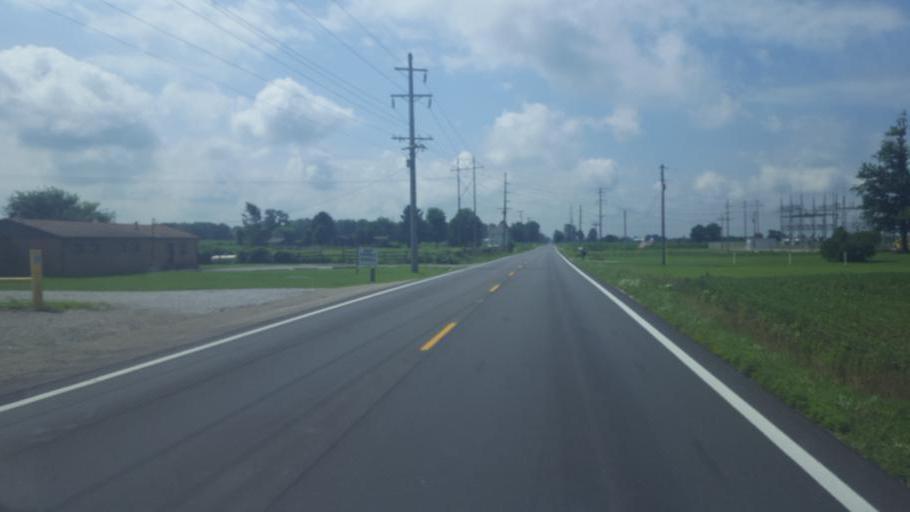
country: US
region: Ohio
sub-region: Fairfield County
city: Millersport
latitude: 39.8913
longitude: -82.5645
